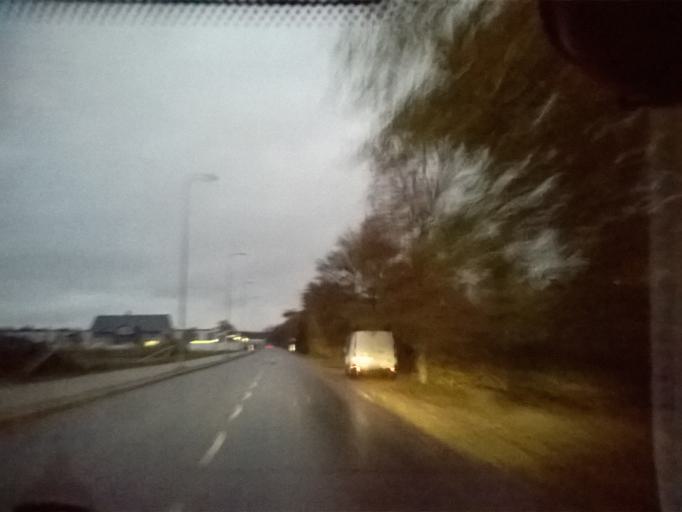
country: EE
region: Harju
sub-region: Viimsi vald
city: Haabneeme
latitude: 59.5180
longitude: 24.8251
